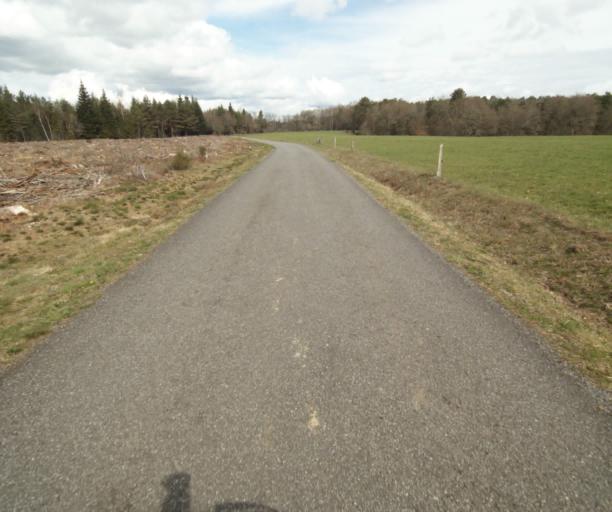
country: FR
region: Limousin
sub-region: Departement de la Correze
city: Correze
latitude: 45.3536
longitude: 1.9560
